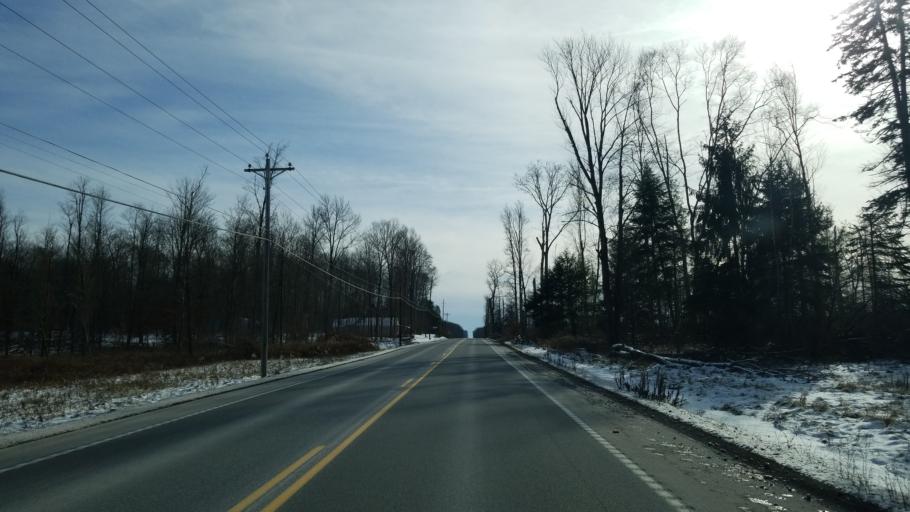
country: US
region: Pennsylvania
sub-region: Clearfield County
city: Clearfield
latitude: 41.1498
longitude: -78.5471
